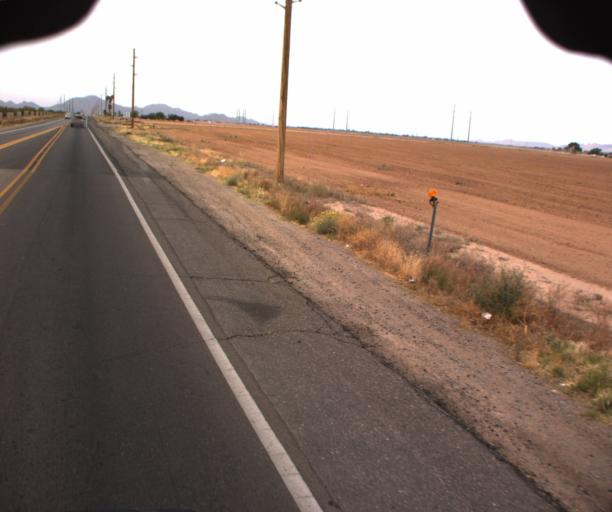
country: US
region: Arizona
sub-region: Pinal County
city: Coolidge
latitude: 33.0026
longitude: -111.5258
